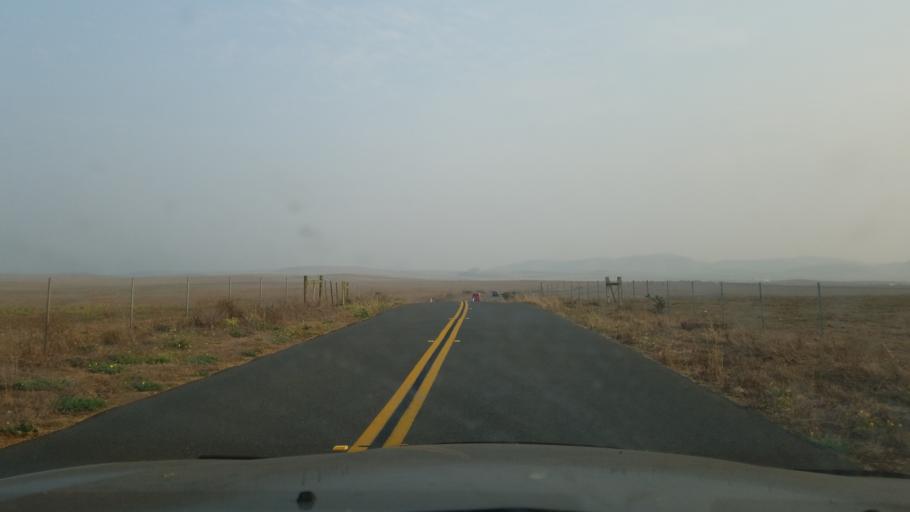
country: US
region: California
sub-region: Marin County
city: Inverness
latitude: 38.1358
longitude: -122.9353
